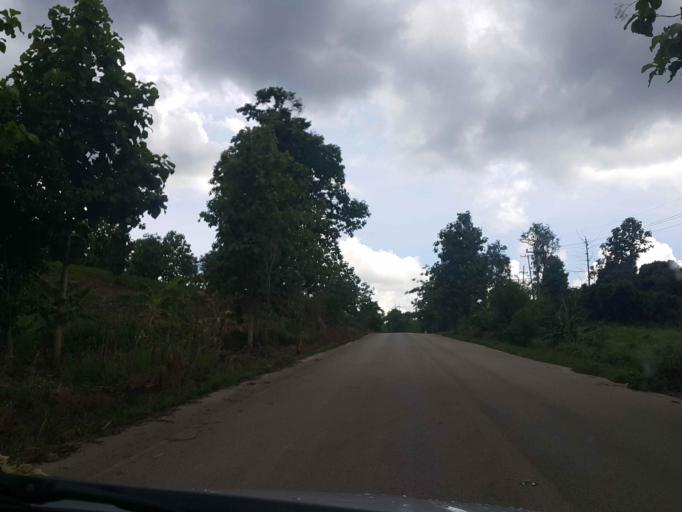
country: TH
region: Phayao
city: Dok Kham Tai
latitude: 18.9605
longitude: 100.0744
